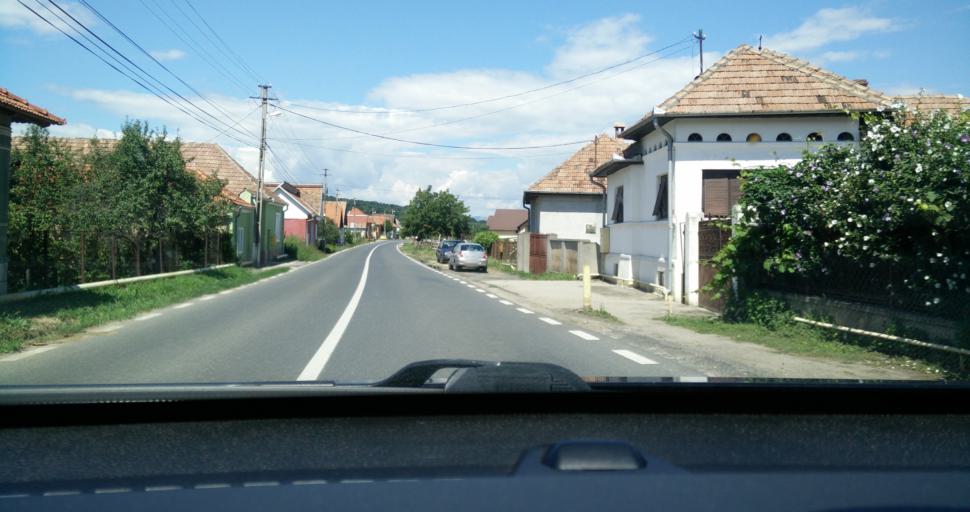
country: RO
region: Alba
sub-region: Comuna Sasciori
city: Sebesel
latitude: 45.8899
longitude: 23.5632
